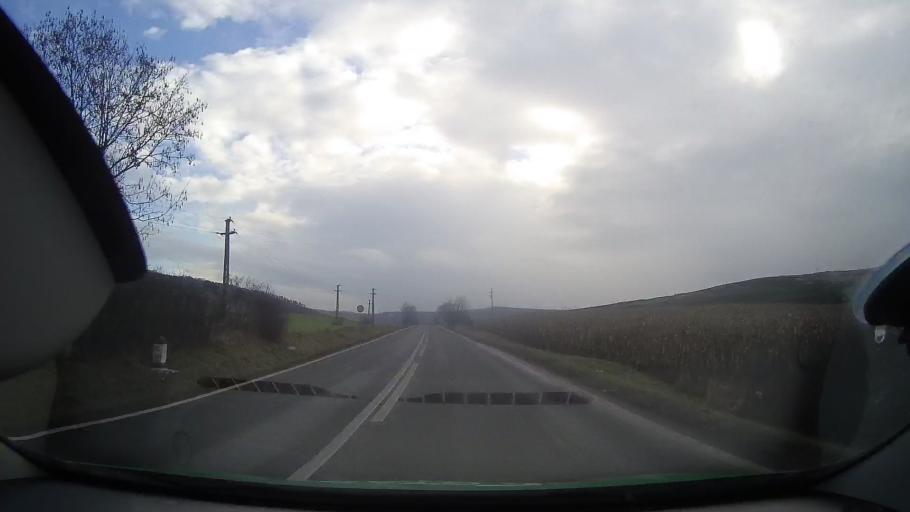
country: RO
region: Mures
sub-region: Comuna Cucerdea
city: Cucerdea
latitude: 46.3790
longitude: 24.2559
